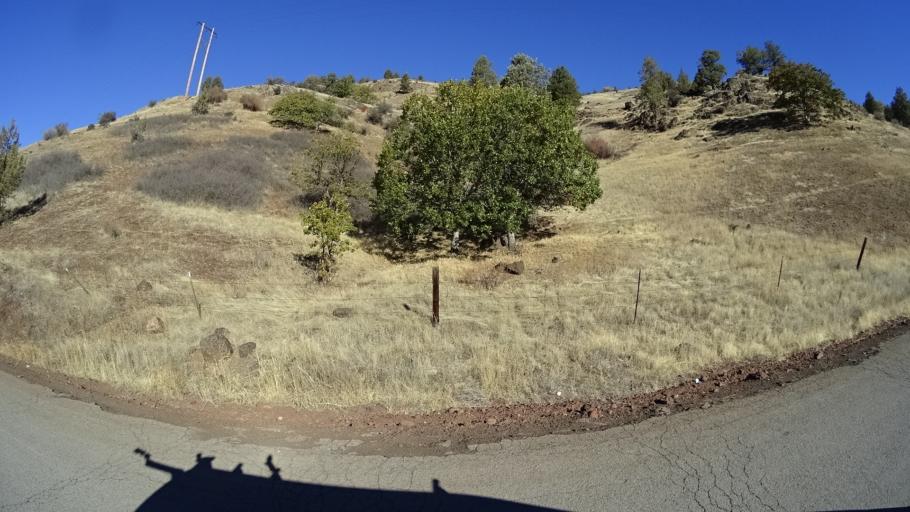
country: US
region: California
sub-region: Siskiyou County
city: Montague
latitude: 41.9691
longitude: -122.3885
